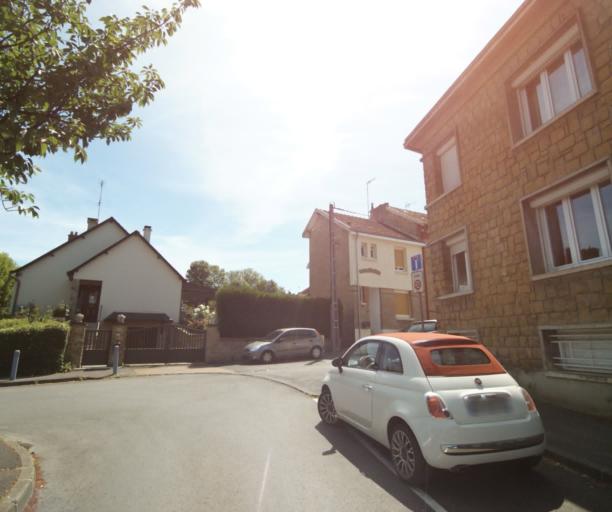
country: FR
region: Champagne-Ardenne
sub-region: Departement des Ardennes
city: Charleville-Mezieres
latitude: 49.7540
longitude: 4.7245
